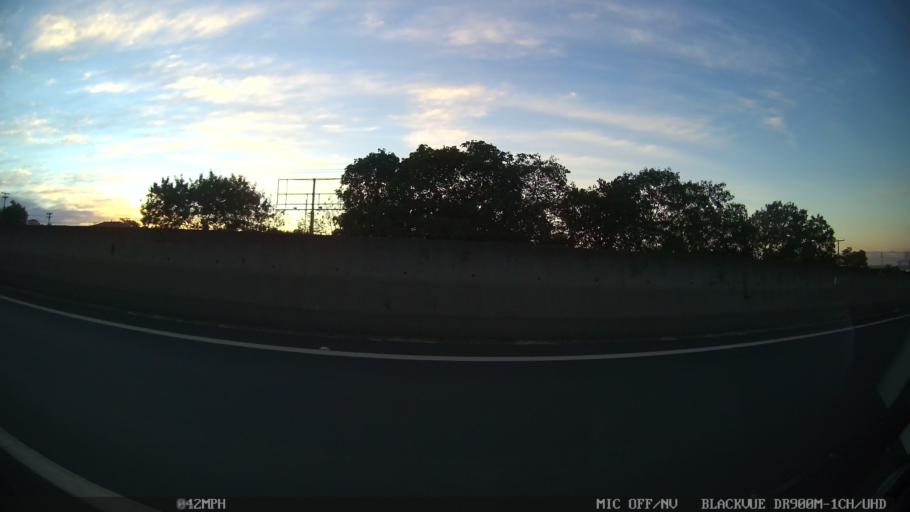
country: BR
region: Sao Paulo
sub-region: Catanduva
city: Catanduva
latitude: -21.1298
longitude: -49.0112
